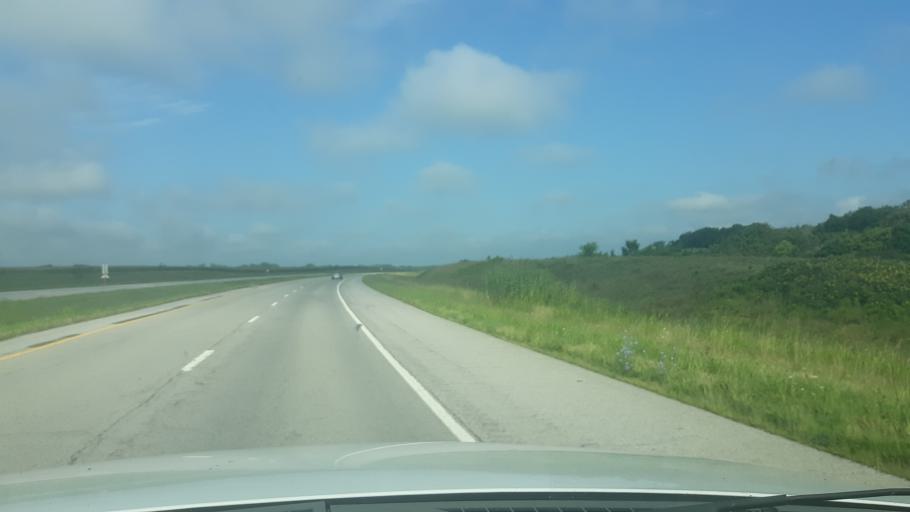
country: US
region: Illinois
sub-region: Saline County
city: Harrisburg
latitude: 37.7301
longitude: -88.5958
